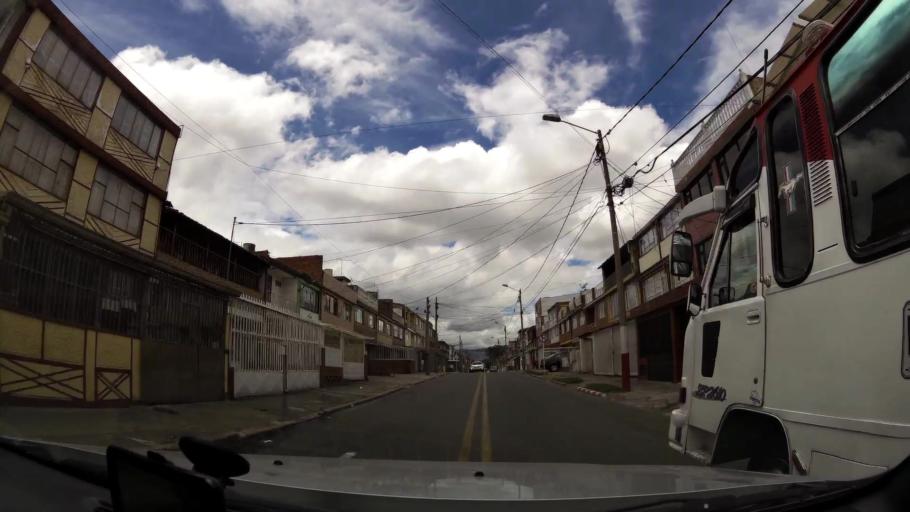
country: CO
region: Bogota D.C.
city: Bogota
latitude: 4.6053
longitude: -74.1068
